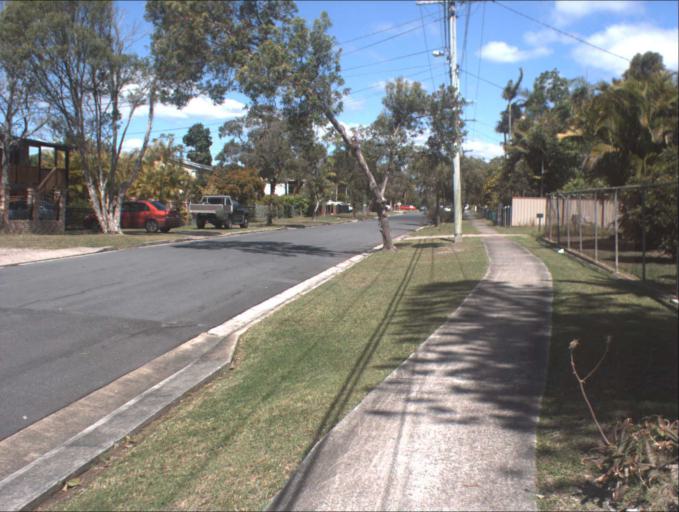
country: AU
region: Queensland
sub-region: Logan
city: Logan City
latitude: -27.6708
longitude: 153.1048
